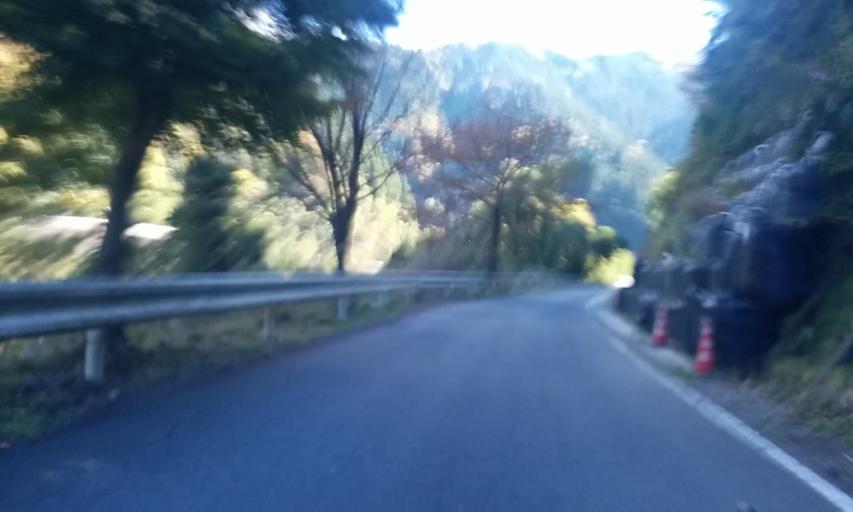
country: JP
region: Kyoto
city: Kameoka
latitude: 35.1304
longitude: 135.5640
